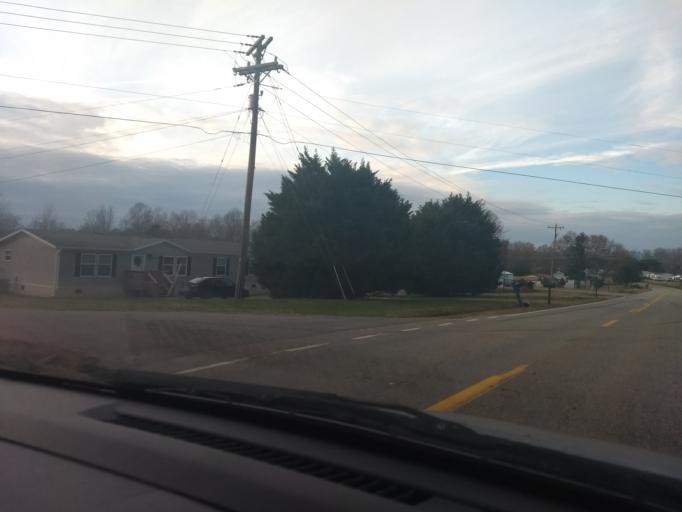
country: US
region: South Carolina
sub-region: Greenville County
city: Greer
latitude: 34.9899
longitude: -82.2024
